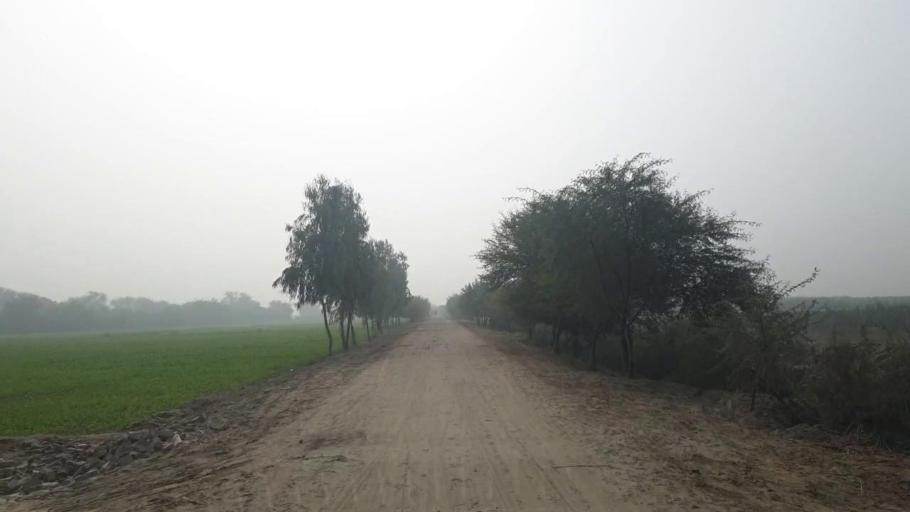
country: PK
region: Sindh
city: Bhit Shah
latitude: 25.7942
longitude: 68.5737
